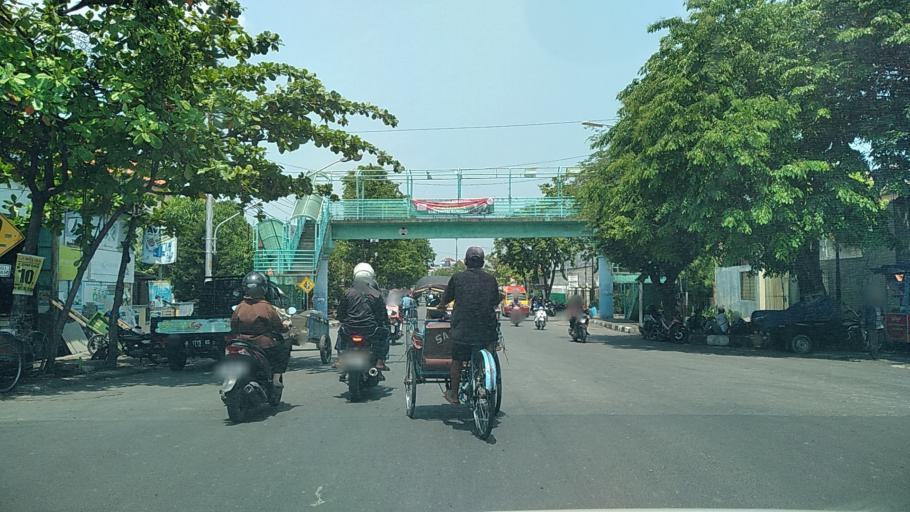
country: ID
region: Central Java
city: Semarang
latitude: -6.9704
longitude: 110.4387
